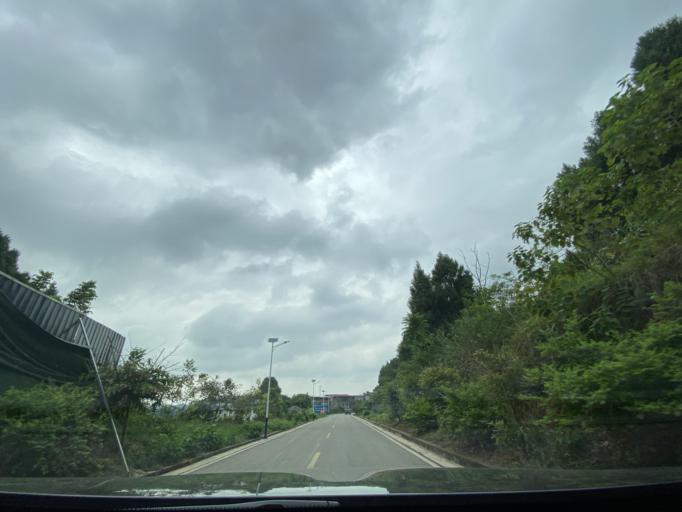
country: CN
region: Sichuan
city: Jiancheng
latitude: 30.5395
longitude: 104.5222
